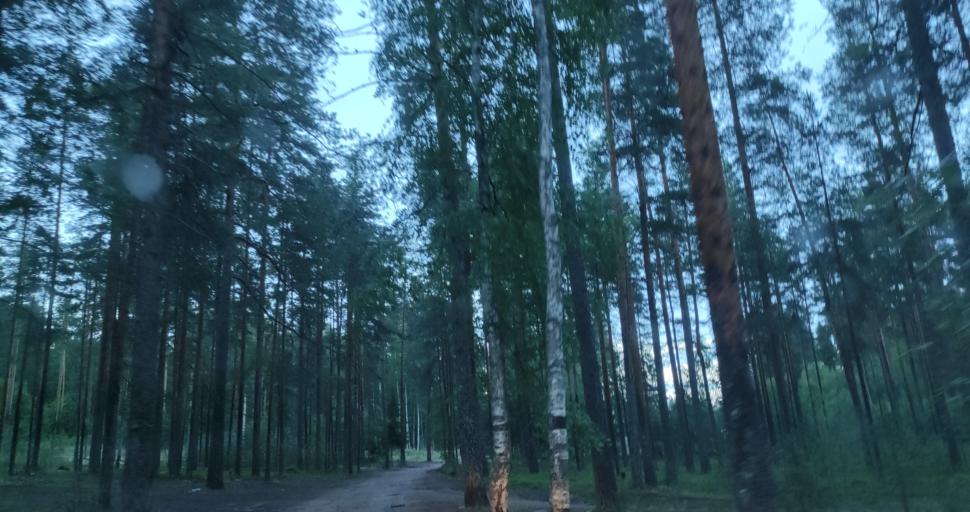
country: RU
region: Leningrad
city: Sapernoye
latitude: 60.6754
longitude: 29.9349
